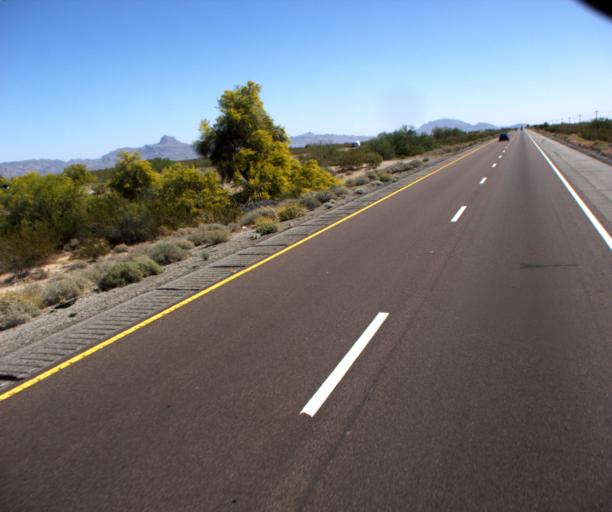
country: US
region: Arizona
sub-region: La Paz County
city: Salome
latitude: 33.5603
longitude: -113.2974
